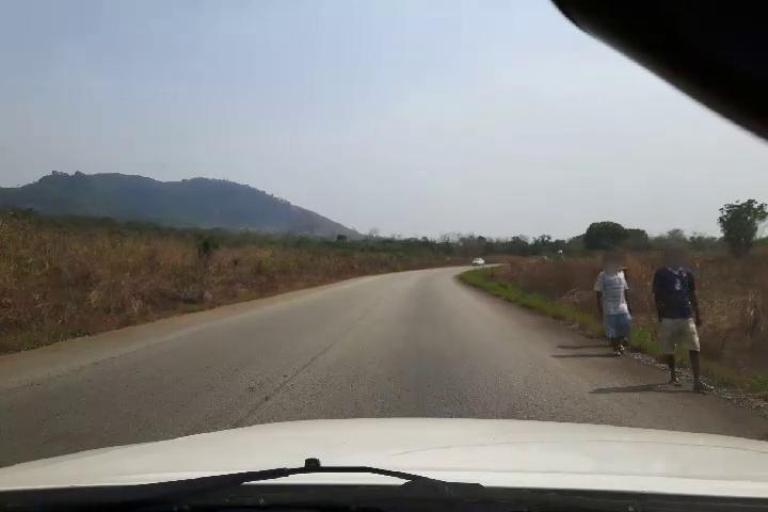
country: SL
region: Northern Province
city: Yonibana
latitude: 8.3826
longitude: -12.1967
